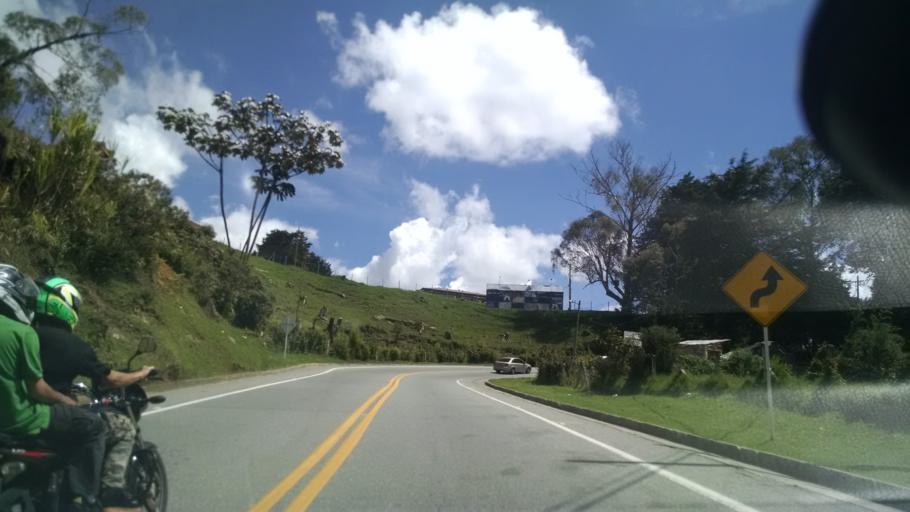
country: CO
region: Antioquia
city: Envigado
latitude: 6.1413
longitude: -75.5222
